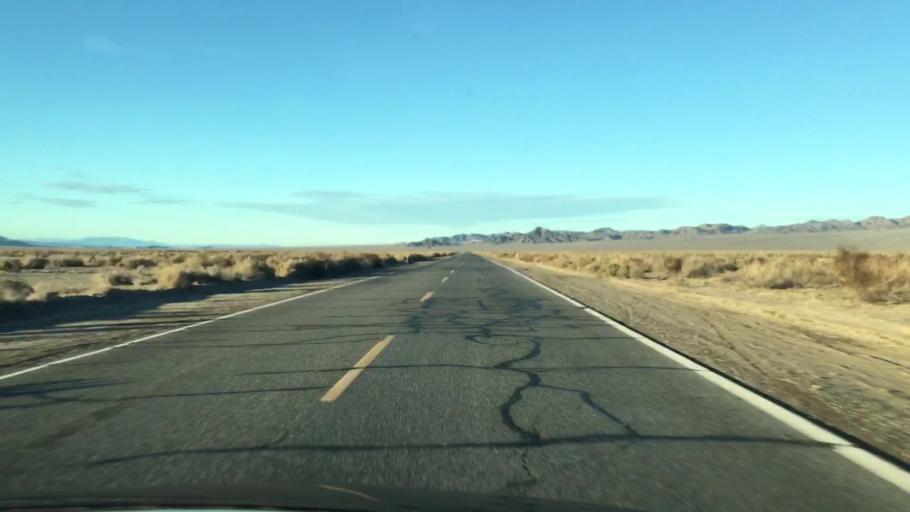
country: US
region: California
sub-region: San Bernardino County
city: Fort Irwin
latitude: 35.2981
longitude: -116.0829
